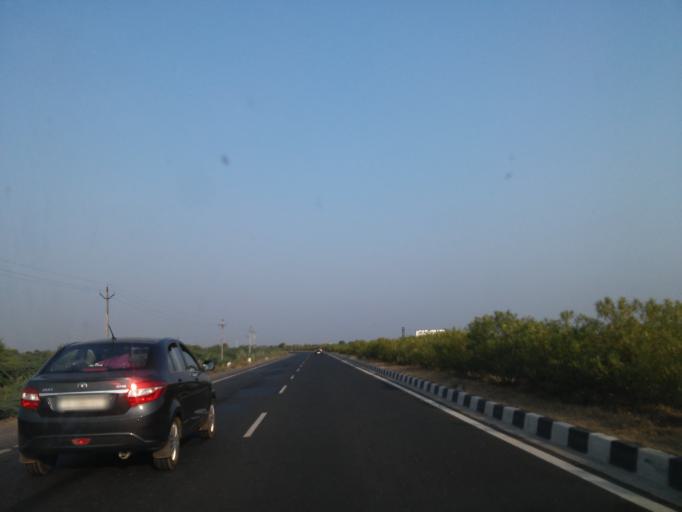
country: IN
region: Gujarat
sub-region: Ahmadabad
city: Sanand
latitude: 23.0768
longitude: 72.1791
